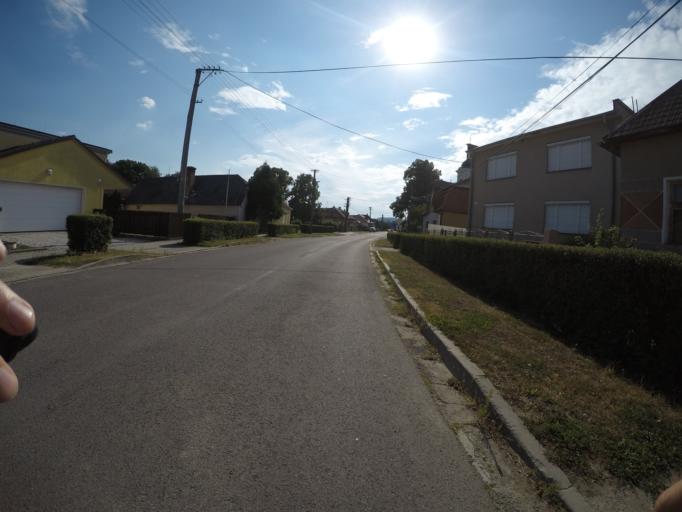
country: SK
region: Trenciansky
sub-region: Okres Trencin
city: Trencin
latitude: 48.8773
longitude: 17.9705
